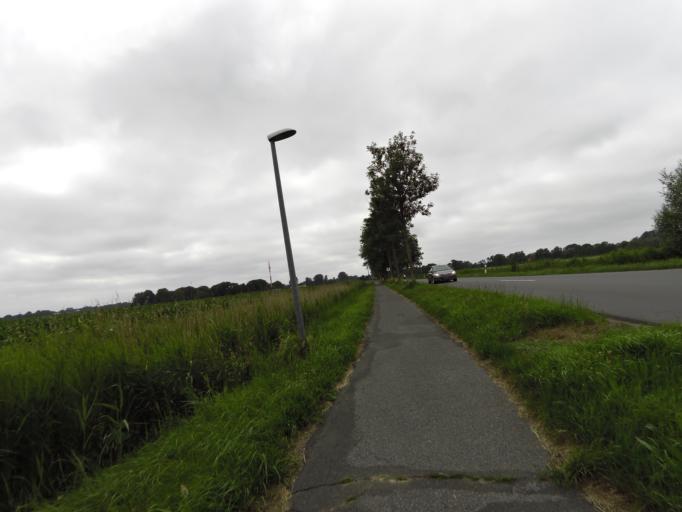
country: DE
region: Lower Saxony
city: Padingbuttel
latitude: 53.7207
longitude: 8.5451
